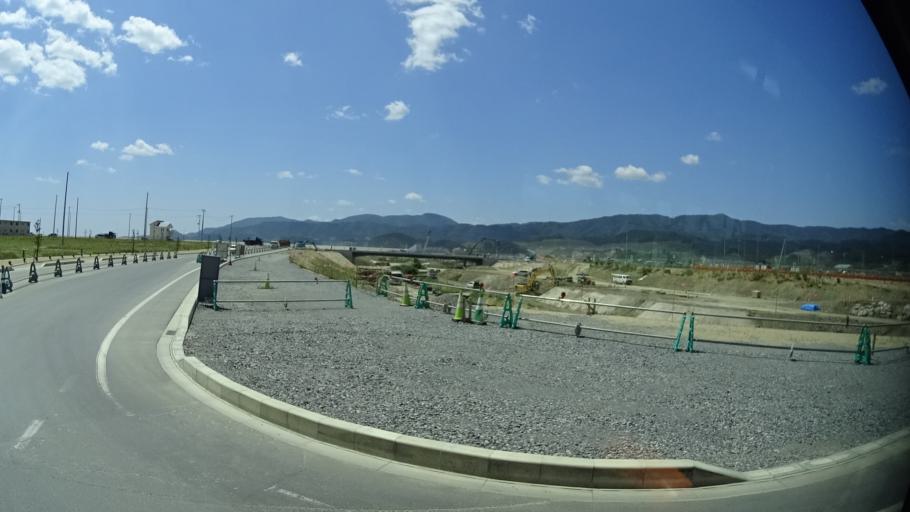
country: JP
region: Iwate
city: Ofunato
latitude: 39.0161
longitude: 141.6336
